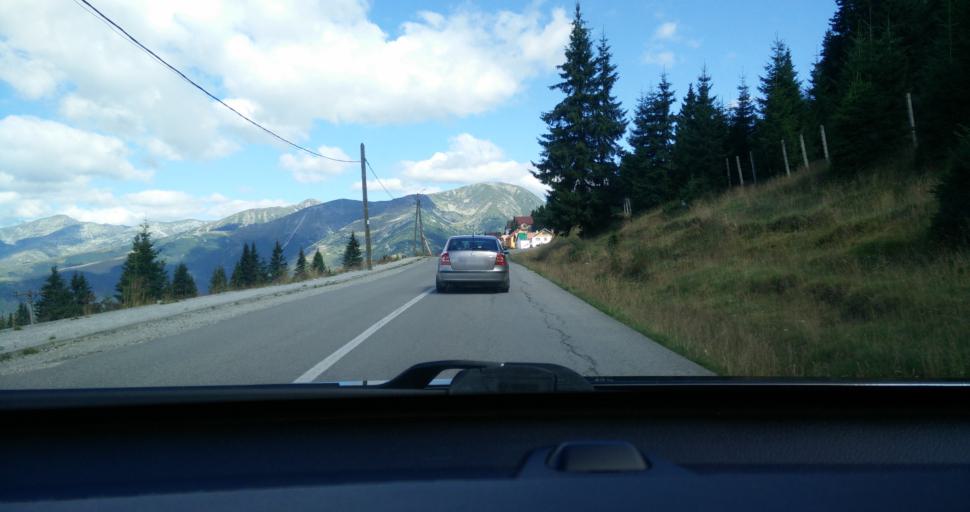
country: RO
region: Gorj
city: Novaci-Straini
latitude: 45.2933
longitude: 23.6861
